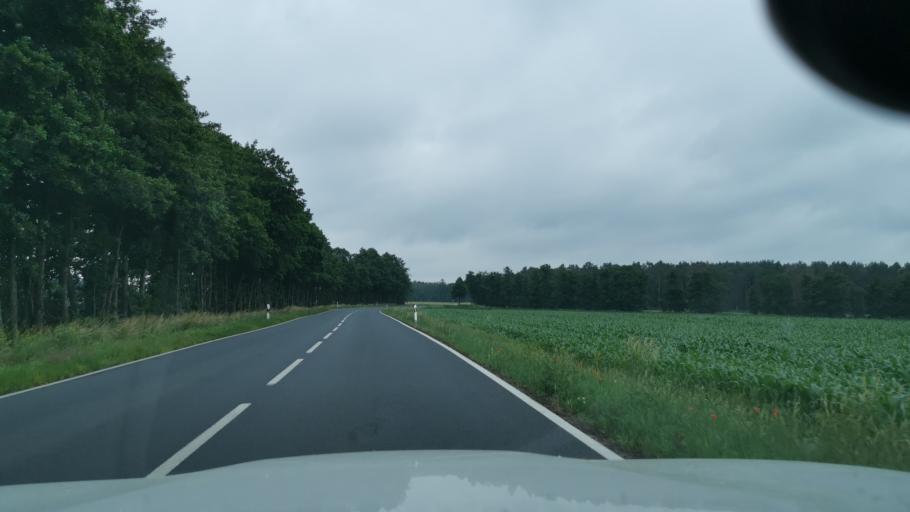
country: DE
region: Saxony-Anhalt
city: Jessen
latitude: 51.8385
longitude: 13.0198
